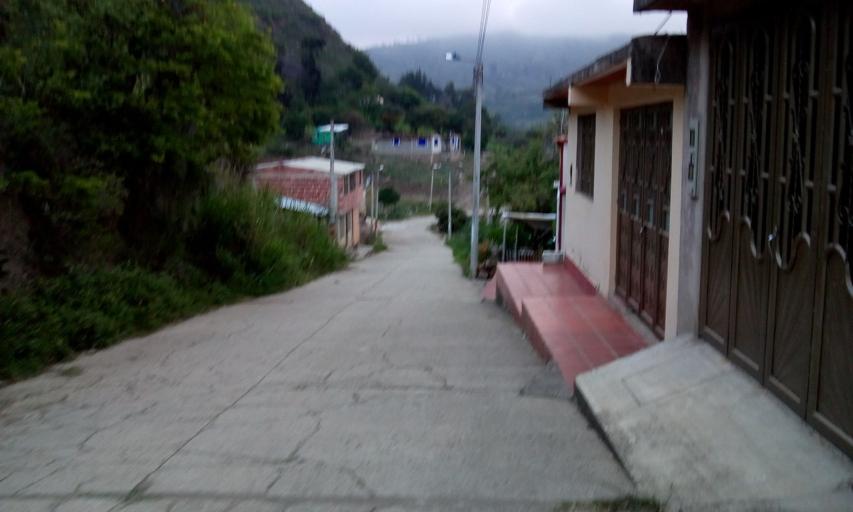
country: CO
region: Boyaca
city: Tipacoque
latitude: 6.4192
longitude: -72.6937
